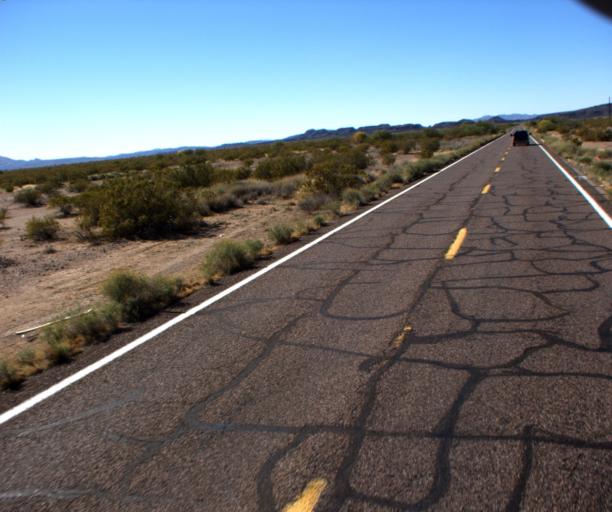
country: US
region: Arizona
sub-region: Pima County
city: Ajo
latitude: 32.6028
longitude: -112.8699
